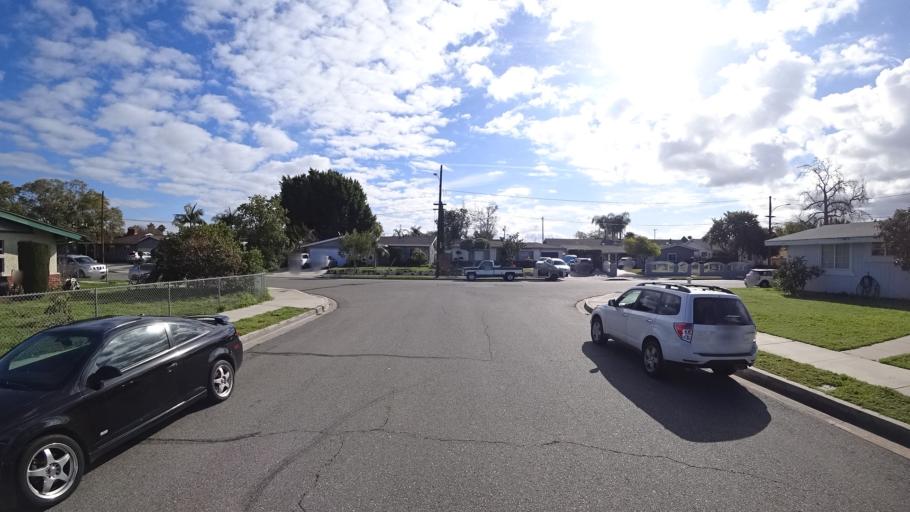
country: US
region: California
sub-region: Orange County
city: Anaheim
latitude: 33.8487
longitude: -117.9026
